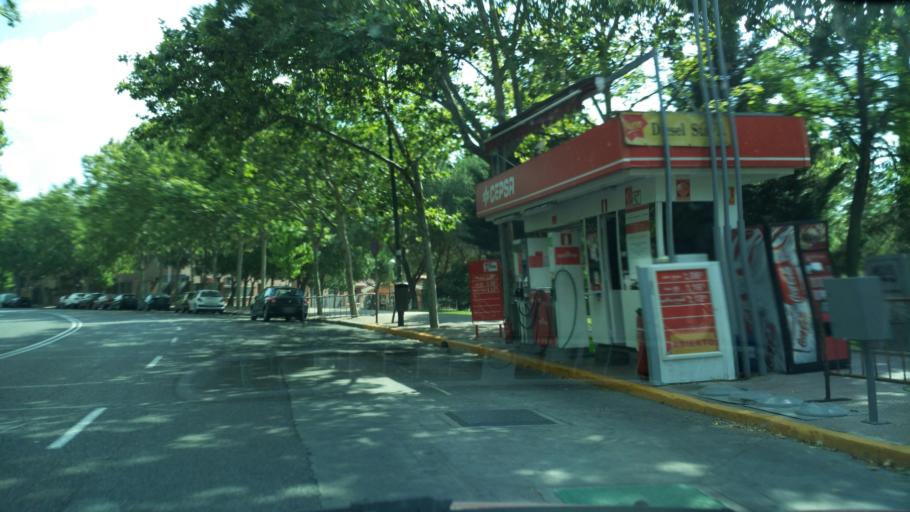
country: ES
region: Madrid
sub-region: Provincia de Madrid
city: Tetuan de las Victorias
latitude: 40.4645
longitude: -3.7198
